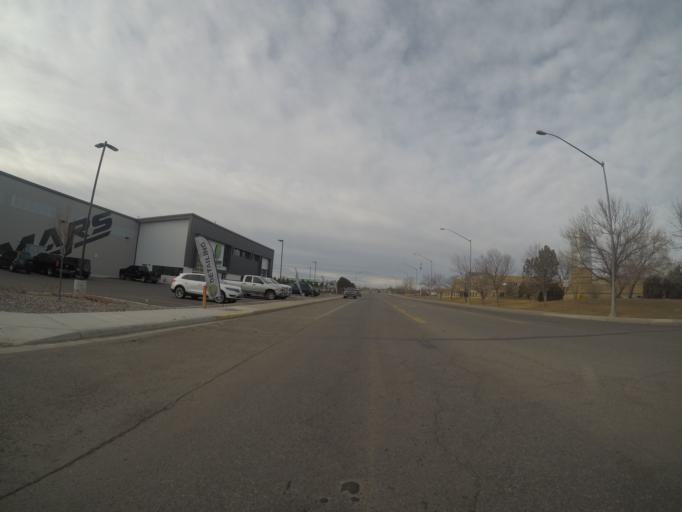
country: US
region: Montana
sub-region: Yellowstone County
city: Billings
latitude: 45.7443
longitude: -108.5876
